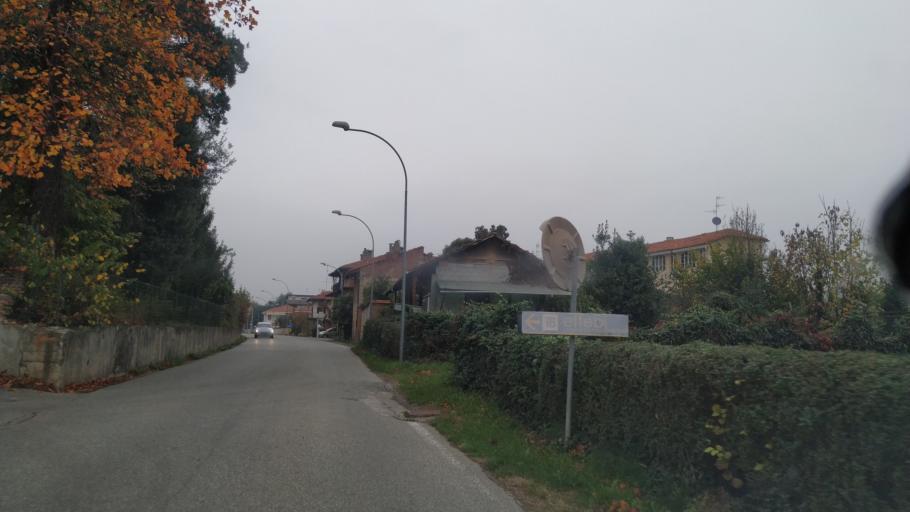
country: IT
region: Piedmont
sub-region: Provincia di Biella
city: Lessona
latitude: 45.5830
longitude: 8.1978
